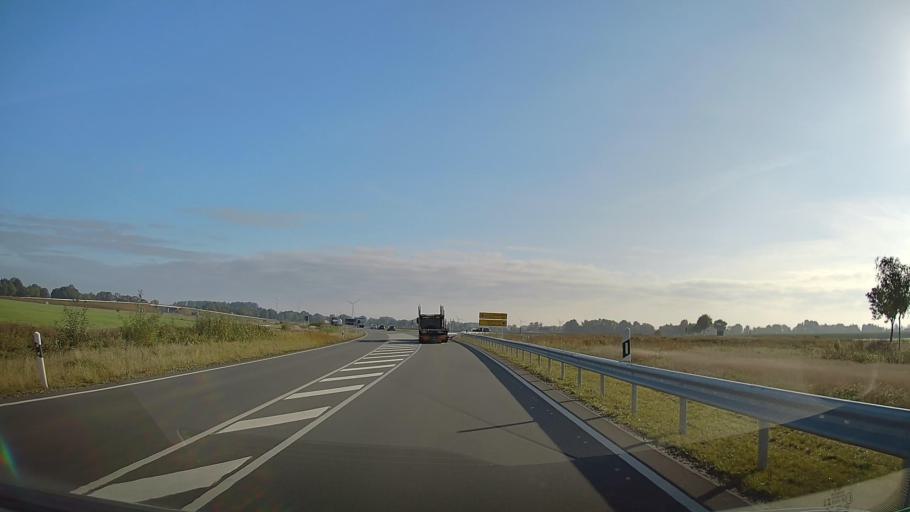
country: DE
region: Lower Saxony
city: Ovelgonne
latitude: 53.2923
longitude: 8.3894
